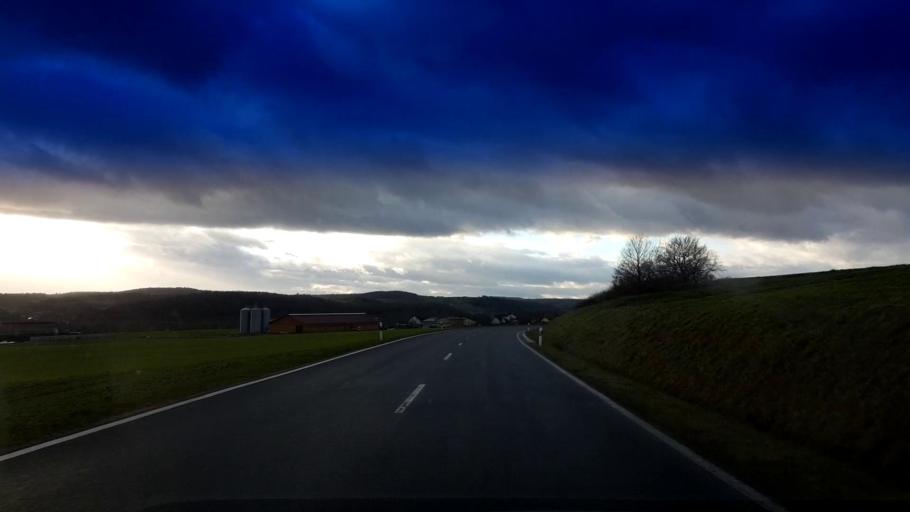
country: DE
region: Bavaria
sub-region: Regierungsbezirk Unterfranken
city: Stettfeld
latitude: 49.9681
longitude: 10.7370
